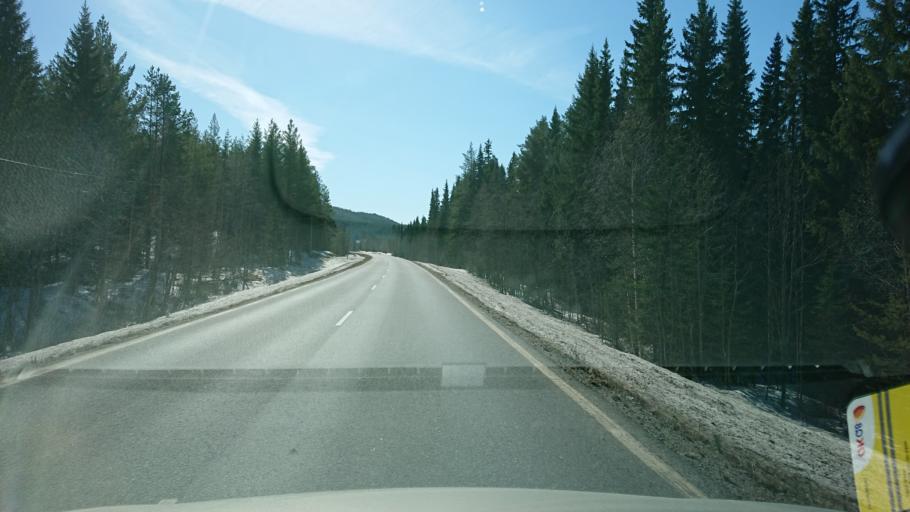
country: SE
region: Vaesterbotten
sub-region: Dorotea Kommun
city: Dorotea
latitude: 64.0658
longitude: 16.2580
